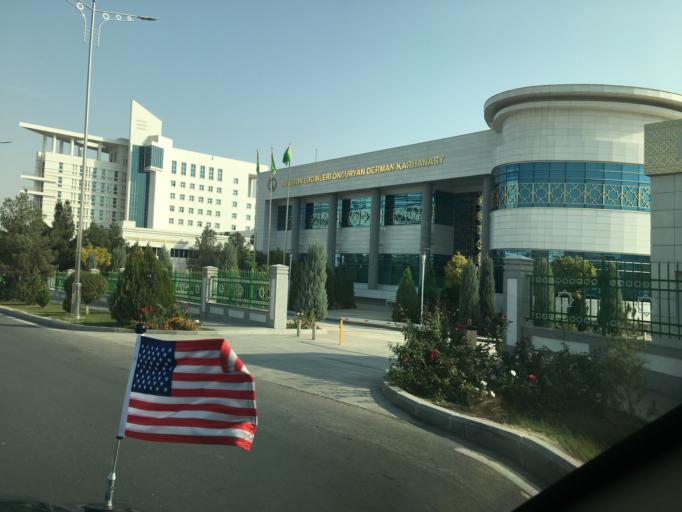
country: TM
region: Ahal
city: Ashgabat
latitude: 37.9497
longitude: 58.3382
